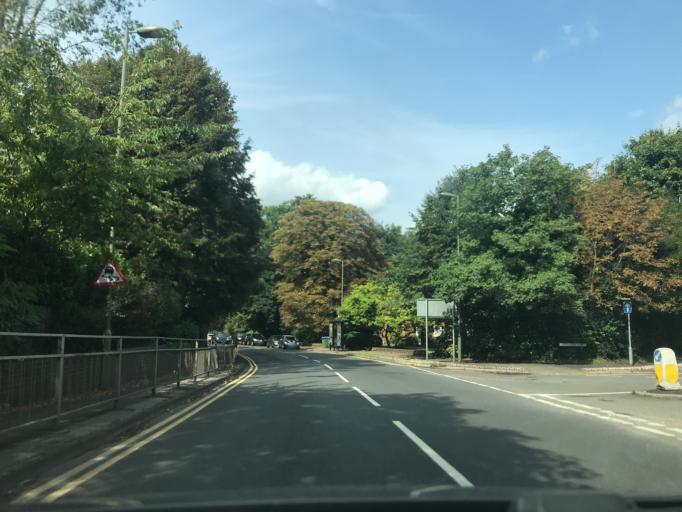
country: GB
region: England
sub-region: Surrey
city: Weybridge
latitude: 51.3676
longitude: -0.4608
